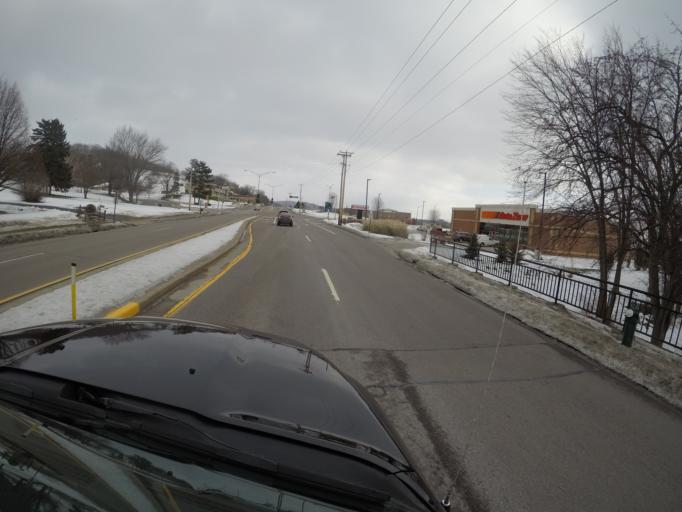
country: US
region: Wisconsin
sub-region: La Crosse County
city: Onalaska
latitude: 43.8806
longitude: -91.2008
